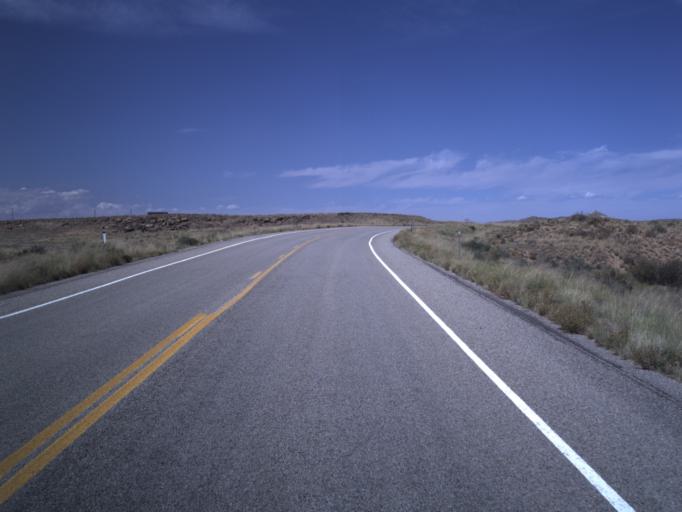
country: US
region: Colorado
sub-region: Montezuma County
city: Towaoc
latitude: 37.1658
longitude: -109.0770
